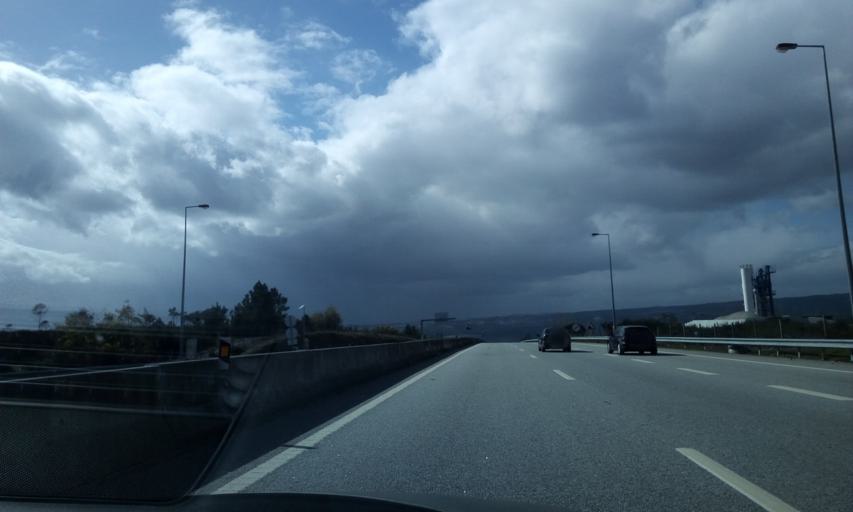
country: PT
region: Viseu
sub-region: Mangualde
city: Mangualde
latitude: 40.6260
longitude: -7.7824
